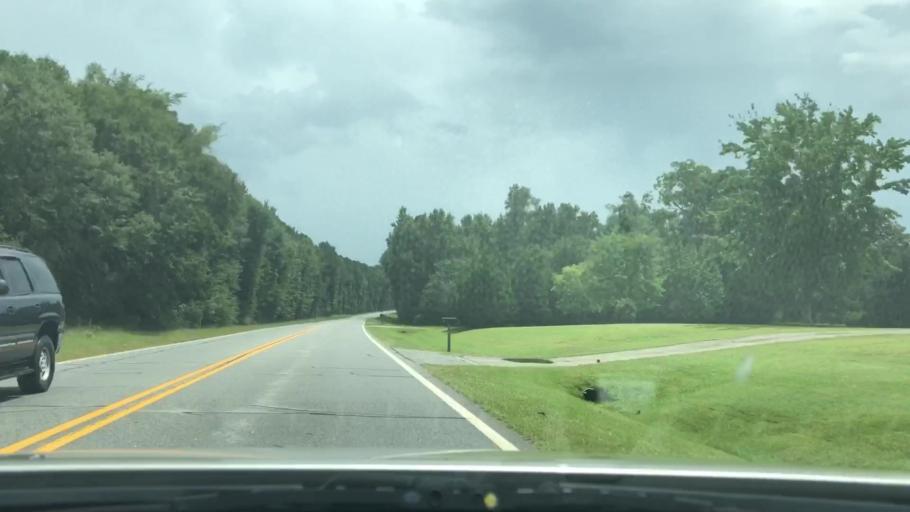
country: US
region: Georgia
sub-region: Pike County
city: Zebulon
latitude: 33.1000
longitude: -84.2920
